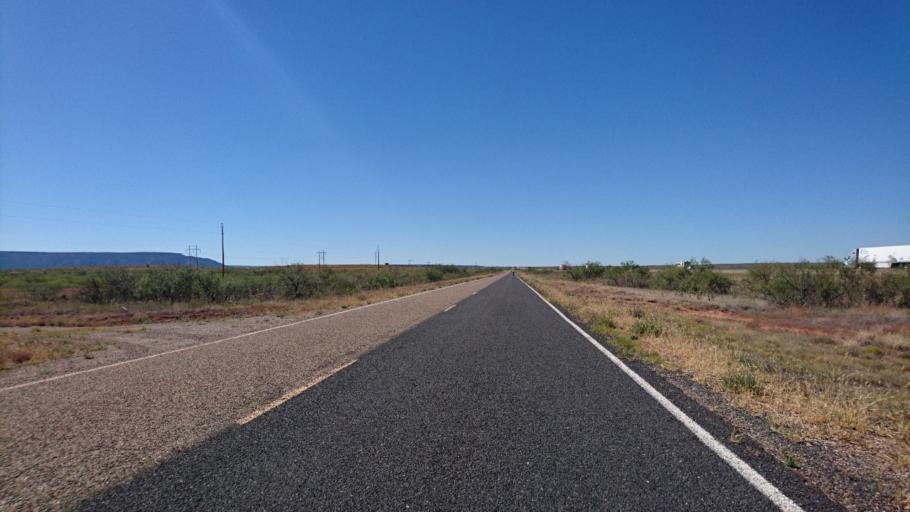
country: US
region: New Mexico
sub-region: Quay County
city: Tucumcari
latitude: 35.0893
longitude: -104.0854
